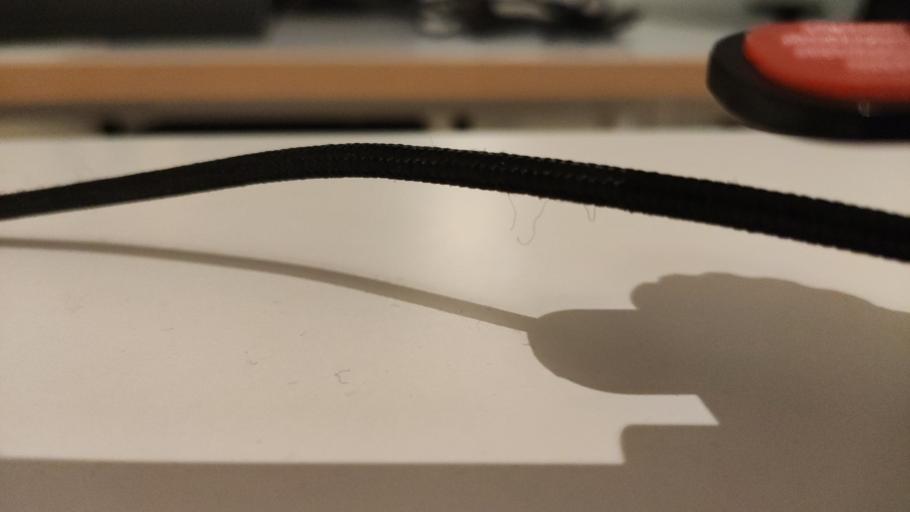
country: RU
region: Moskovskaya
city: Malaya Dubna
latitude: 55.8674
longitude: 38.9639
